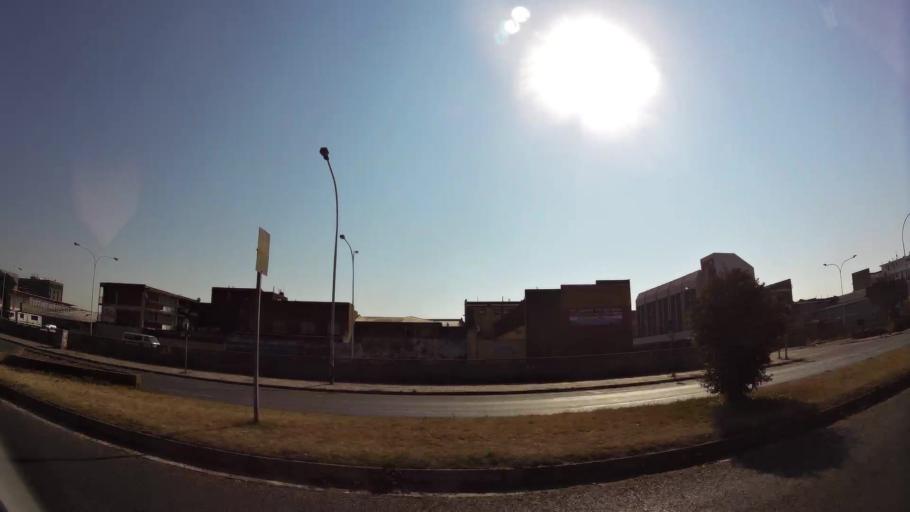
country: ZA
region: Gauteng
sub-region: Ekurhuleni Metropolitan Municipality
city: Boksburg
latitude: -26.2242
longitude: 28.2552
